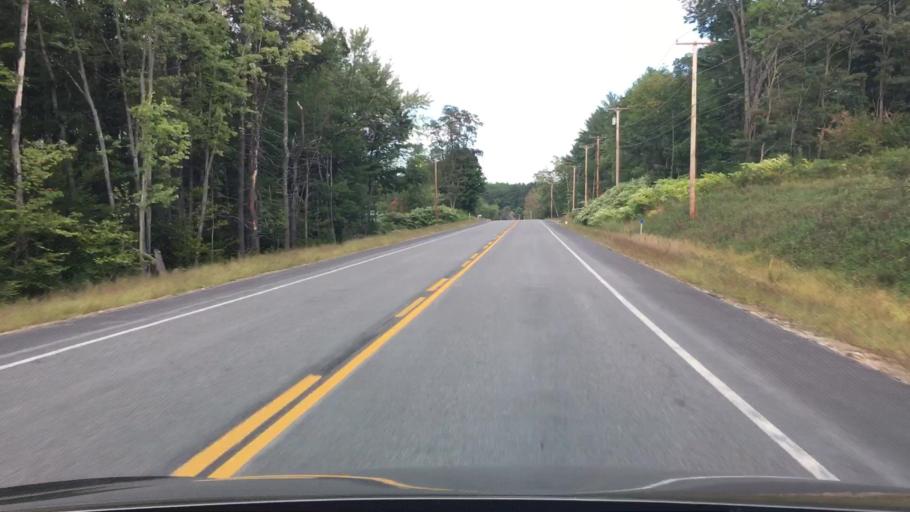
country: US
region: Maine
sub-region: Oxford County
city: Lovell
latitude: 44.0633
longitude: -70.8462
